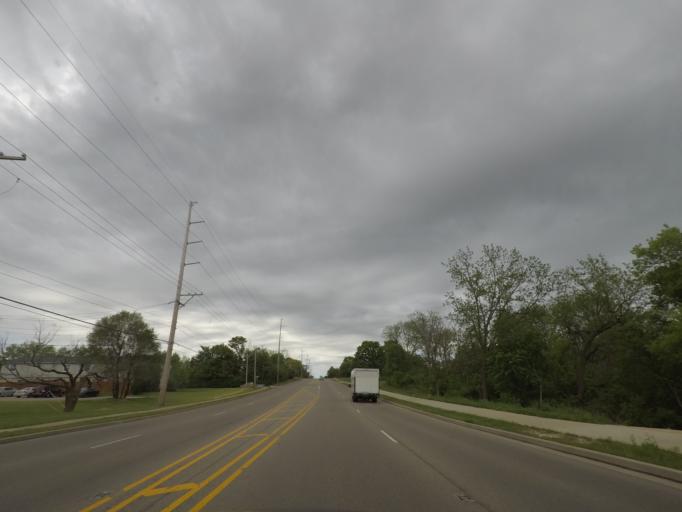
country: US
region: Illinois
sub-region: Winnebago County
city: Loves Park
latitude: 42.2698
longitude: -89.0291
